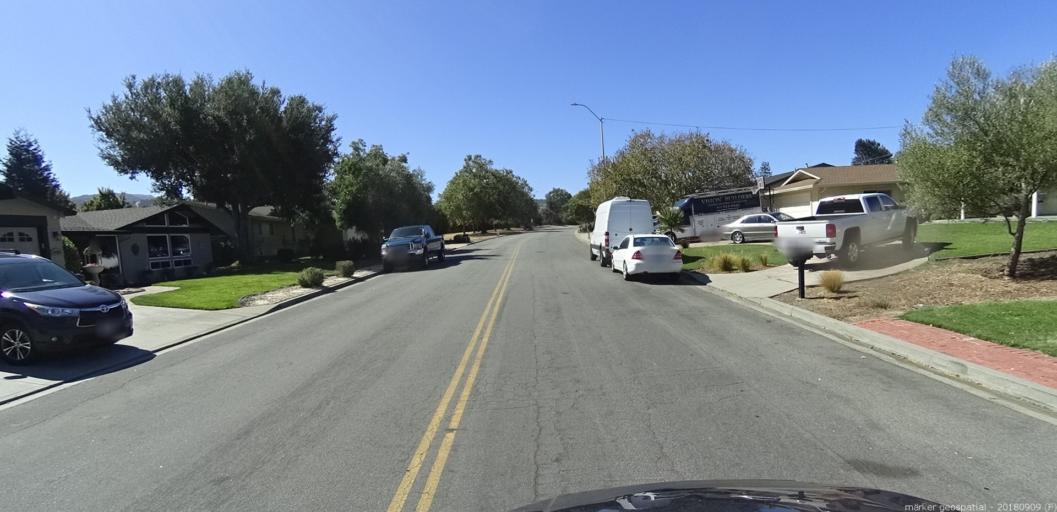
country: US
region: California
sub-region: Monterey County
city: Salinas
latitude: 36.6097
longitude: -121.6925
